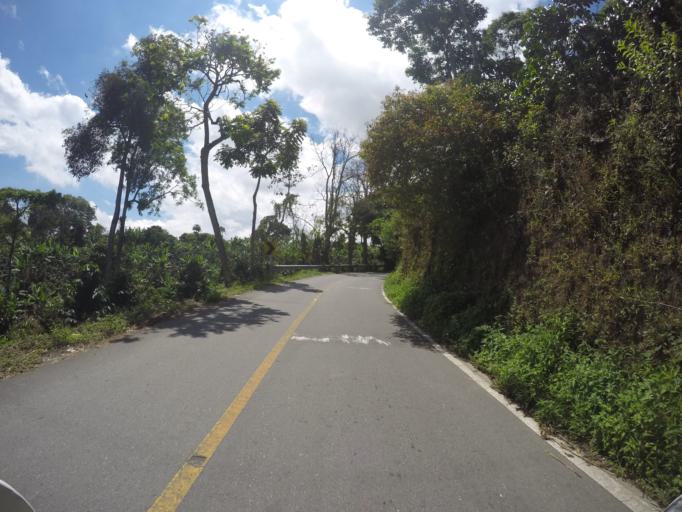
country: CO
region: Quindio
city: Quimbaya
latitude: 4.6300
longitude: -75.7190
